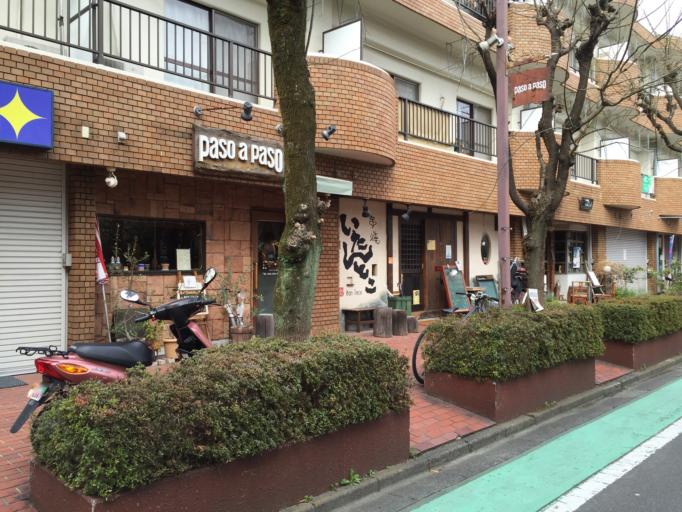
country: JP
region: Tokyo
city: Kokubunji
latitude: 35.6752
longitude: 139.4809
